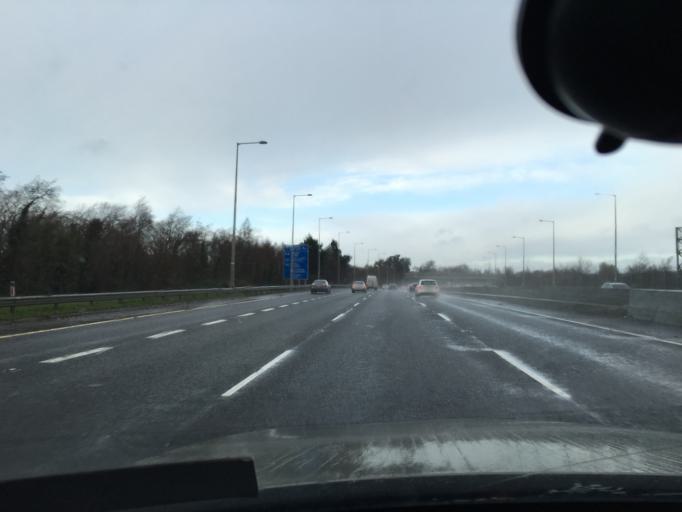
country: IE
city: Cherry Orchard
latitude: 53.3341
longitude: -6.3839
